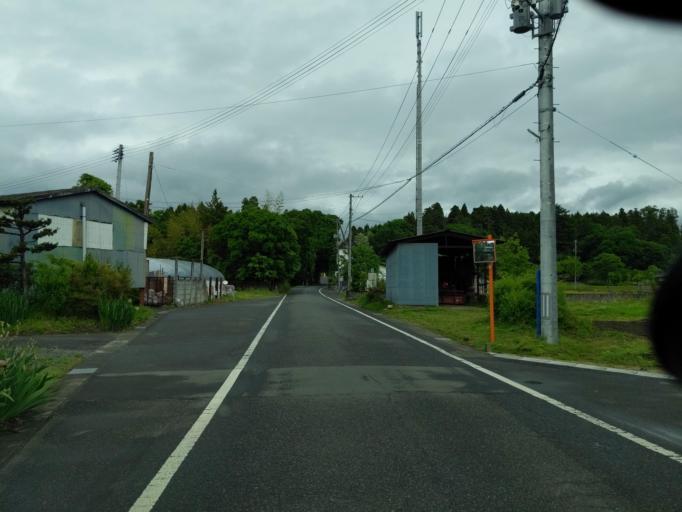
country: JP
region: Fukushima
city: Koriyama
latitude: 37.3580
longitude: 140.4003
